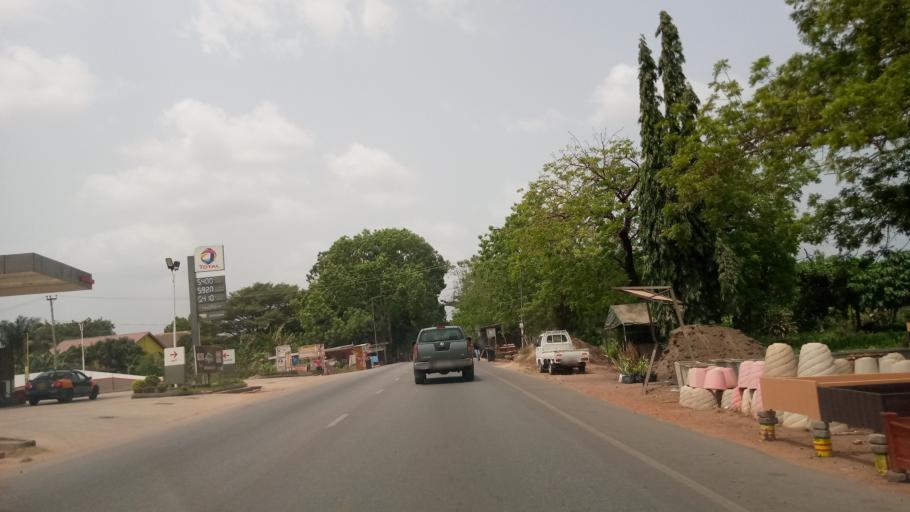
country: GH
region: Greater Accra
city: Dome
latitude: 5.6676
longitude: -0.2177
